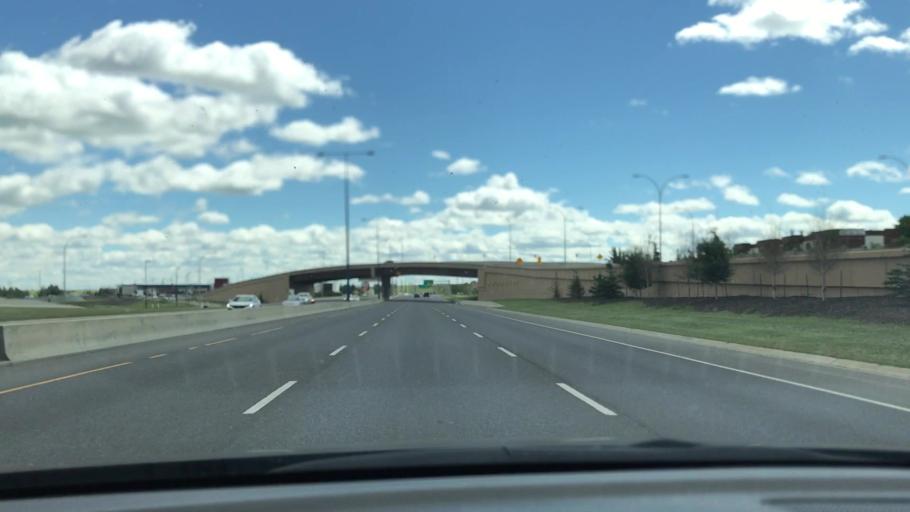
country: CA
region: Alberta
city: Edmonton
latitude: 53.4518
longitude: -113.4927
